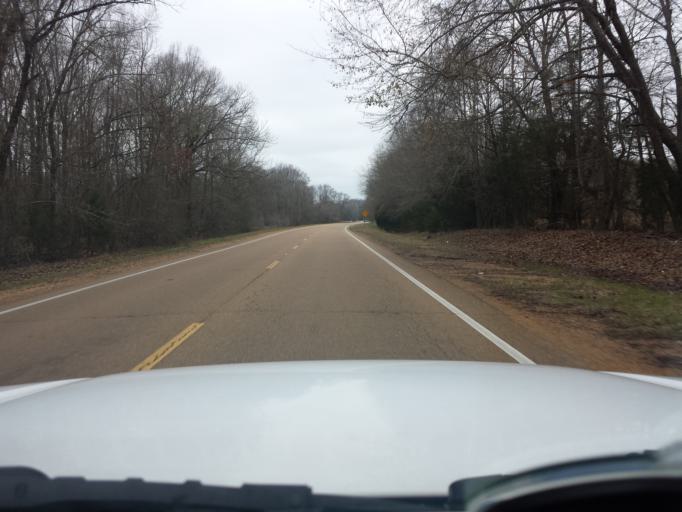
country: US
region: Mississippi
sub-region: Madison County
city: Canton
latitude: 32.7396
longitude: -90.1282
